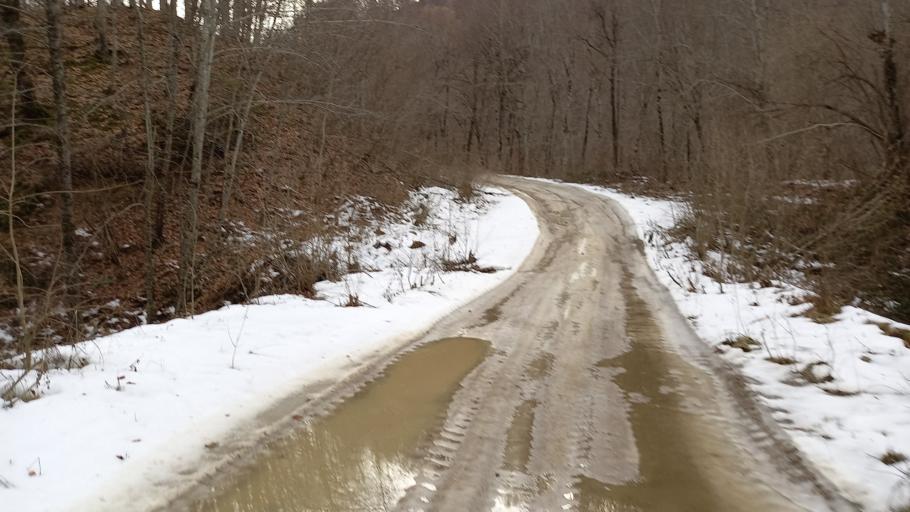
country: RU
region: Adygeya
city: Kamennomostskiy
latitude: 44.1596
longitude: 40.2986
